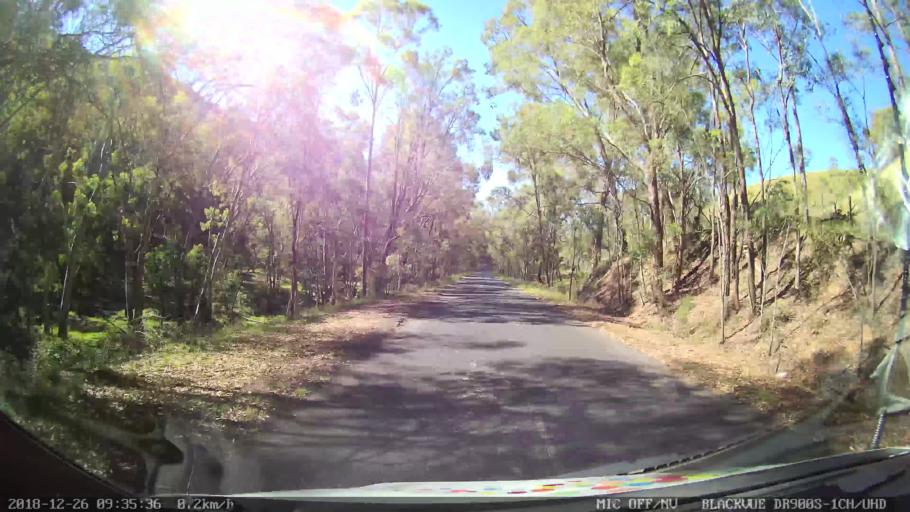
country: AU
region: New South Wales
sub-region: Mid-Western Regional
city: Kandos
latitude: -32.9161
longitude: 150.0414
